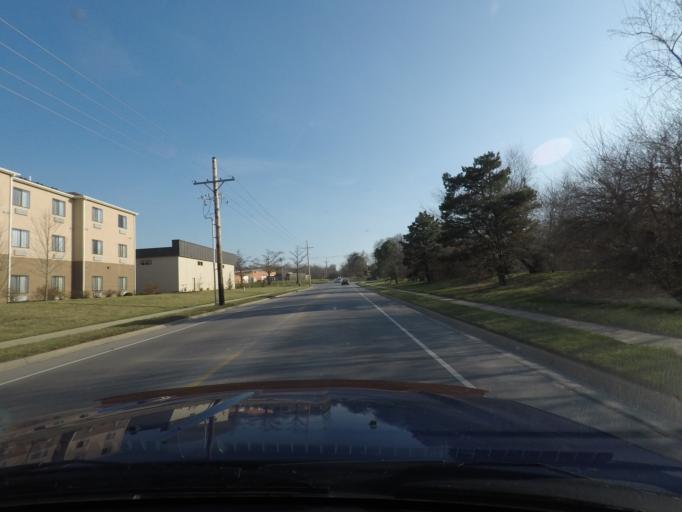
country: US
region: Kansas
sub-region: Douglas County
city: Lawrence
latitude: 38.9816
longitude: -95.2605
